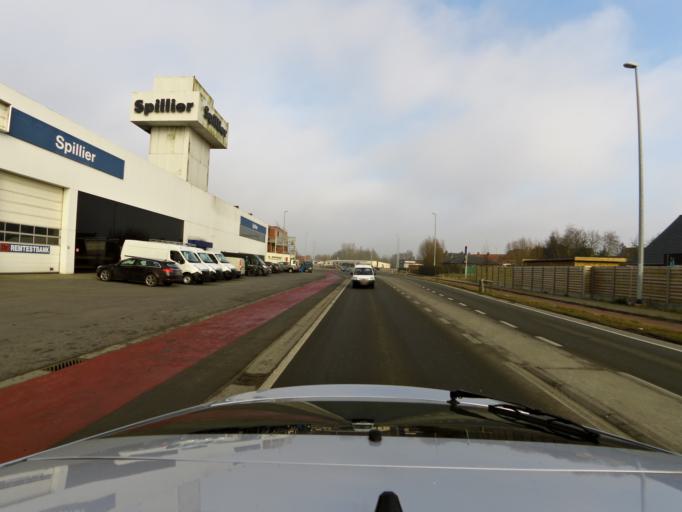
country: BE
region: Flanders
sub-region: Provincie West-Vlaanderen
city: Torhout
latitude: 51.0669
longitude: 3.0921
